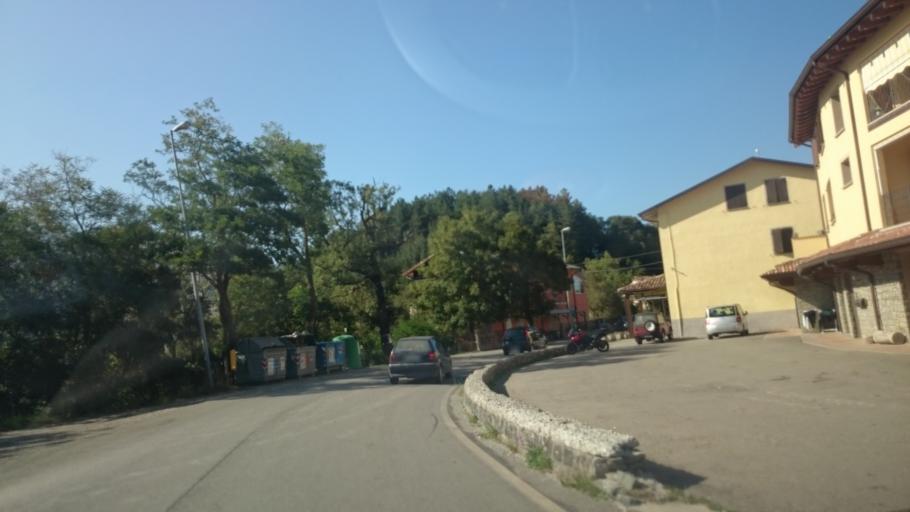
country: IT
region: Emilia-Romagna
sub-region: Provincia di Reggio Emilia
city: Villa Minozzo
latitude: 44.3058
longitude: 10.4614
